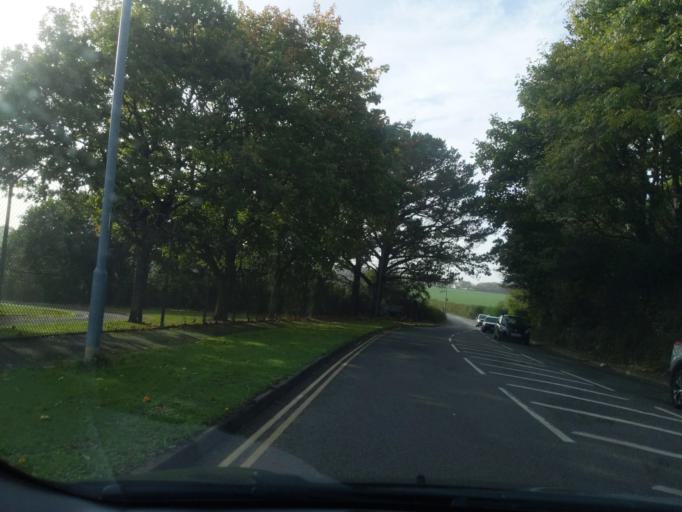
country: GB
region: England
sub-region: Cornwall
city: Torpoint
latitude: 50.3744
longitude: -4.2271
